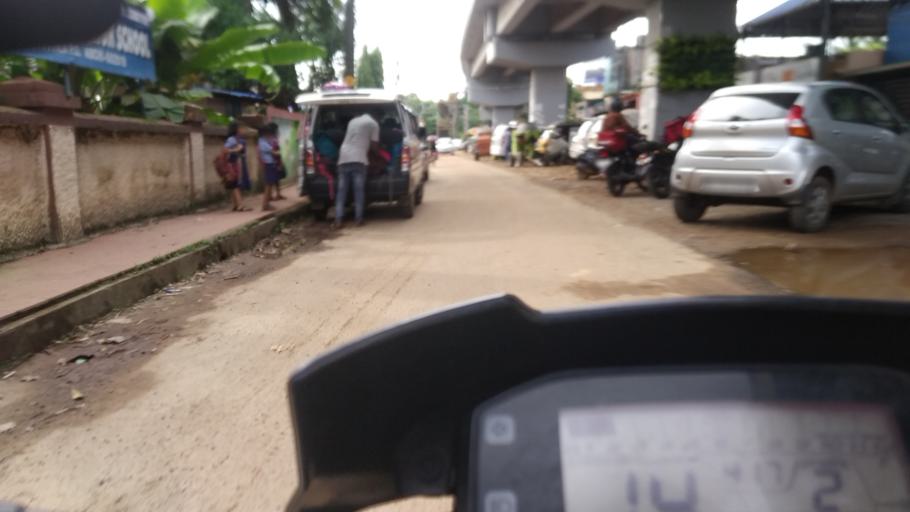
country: IN
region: Kerala
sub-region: Ernakulam
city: Cochin
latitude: 9.9749
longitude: 76.3154
